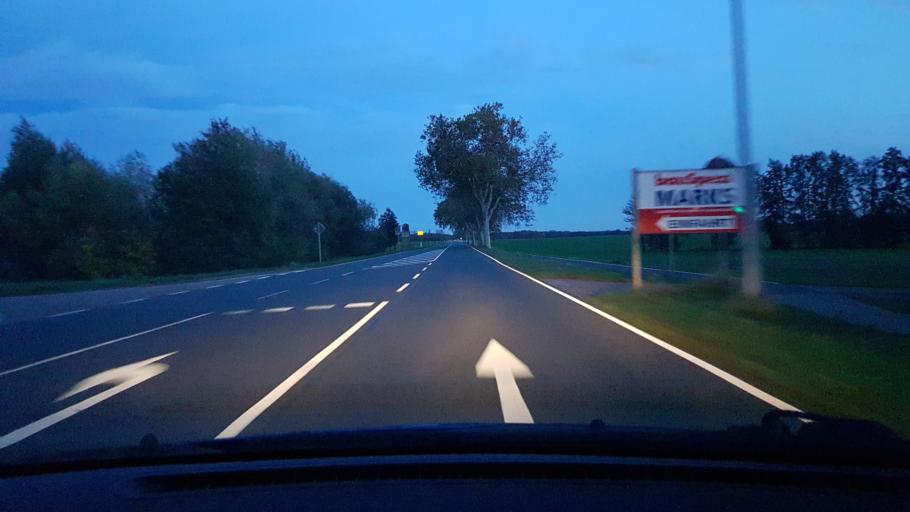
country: DE
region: Saxony-Anhalt
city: Zerbst
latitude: 51.9347
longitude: 12.1312
